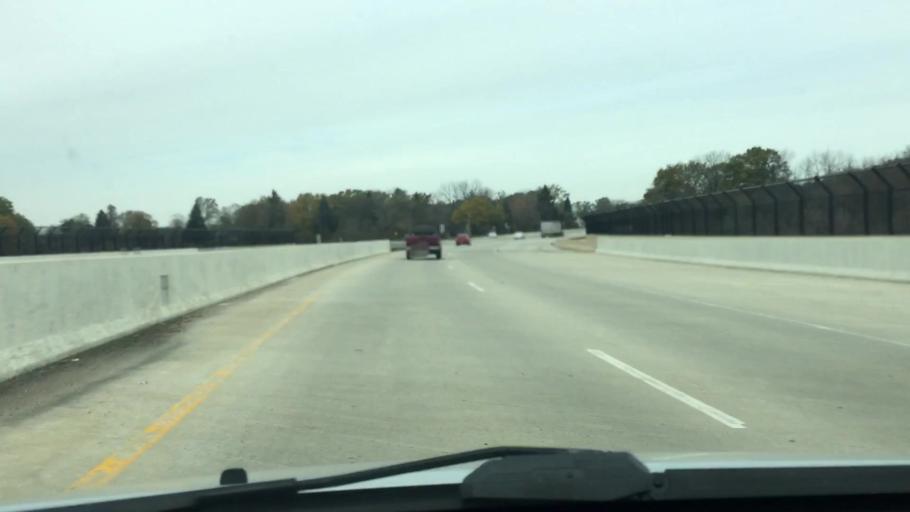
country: US
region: Wisconsin
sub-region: Milwaukee County
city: Hales Corners
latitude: 42.9140
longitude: -88.0445
